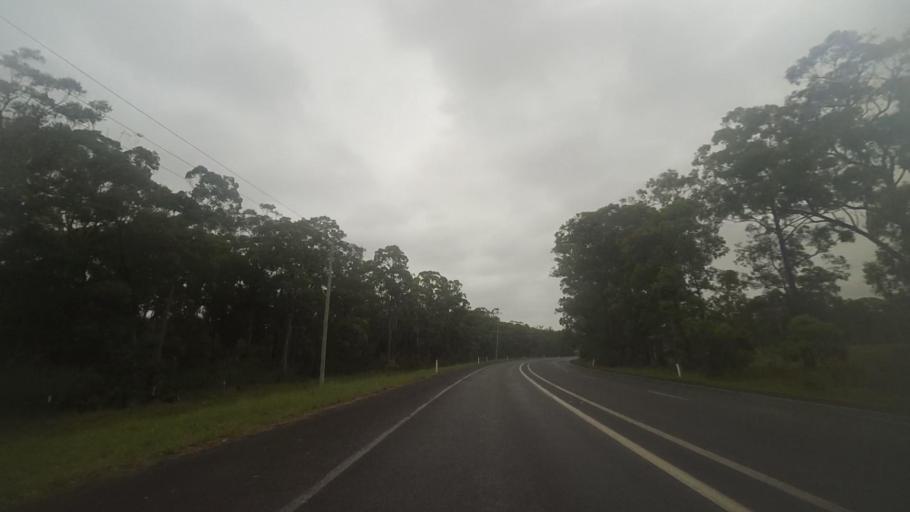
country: AU
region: New South Wales
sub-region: Port Stephens Shire
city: Port Stephens
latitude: -32.6473
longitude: 151.9799
